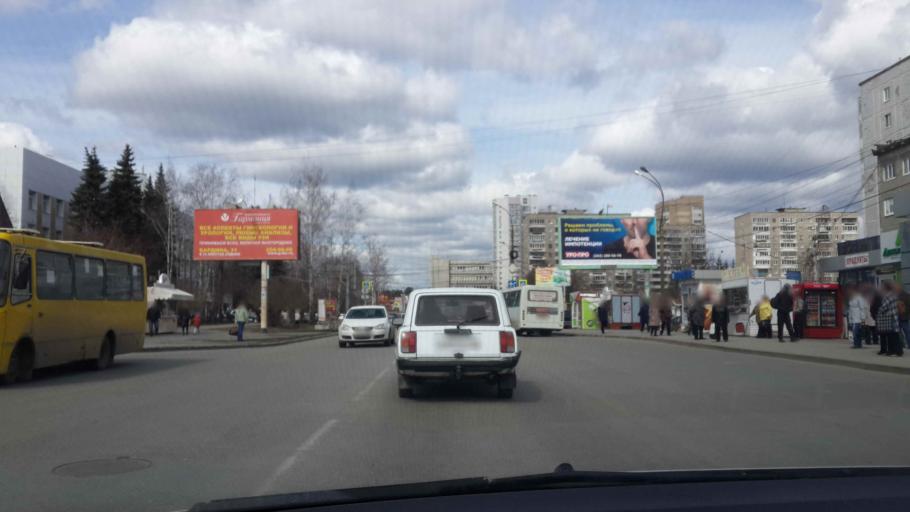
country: RU
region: Sverdlovsk
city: Sovkhoznyy
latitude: 56.8116
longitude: 60.5596
